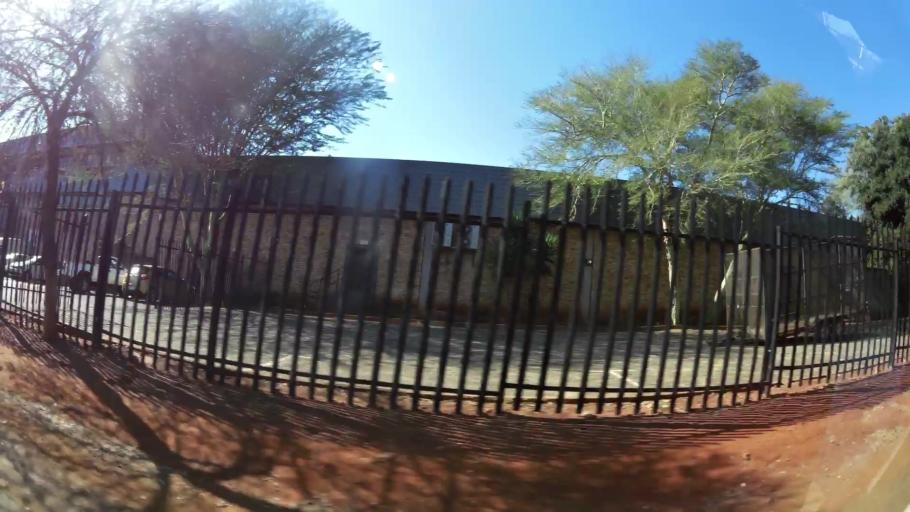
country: ZA
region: Gauteng
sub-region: City of Tshwane Metropolitan Municipality
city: Pretoria
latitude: -25.6790
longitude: 28.2167
